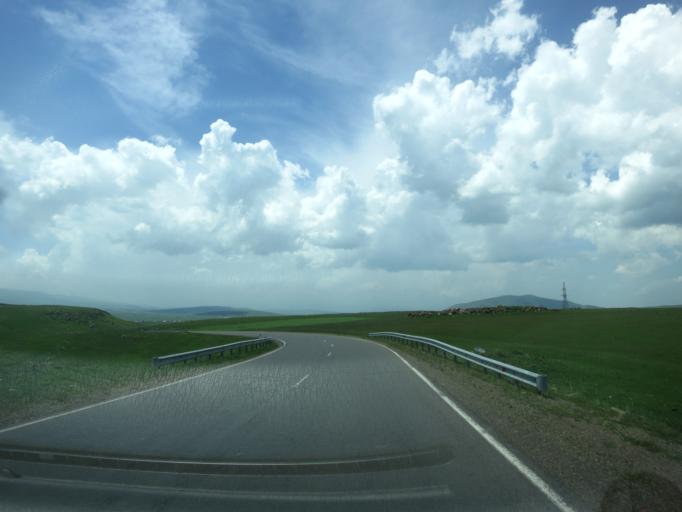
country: GE
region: Samtskhe-Javakheti
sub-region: Ninotsminda
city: Ninotsminda
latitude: 41.2953
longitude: 43.6815
